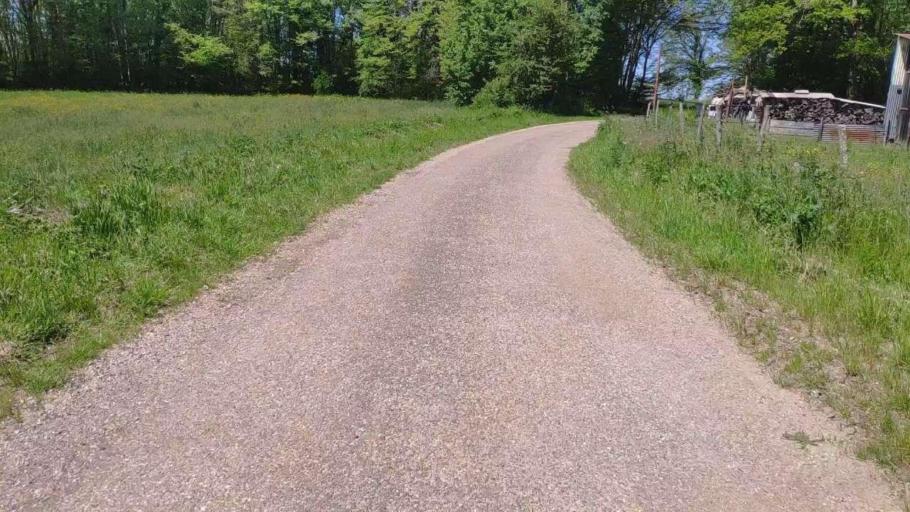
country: FR
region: Franche-Comte
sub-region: Departement du Jura
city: Perrigny
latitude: 46.7166
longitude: 5.6573
